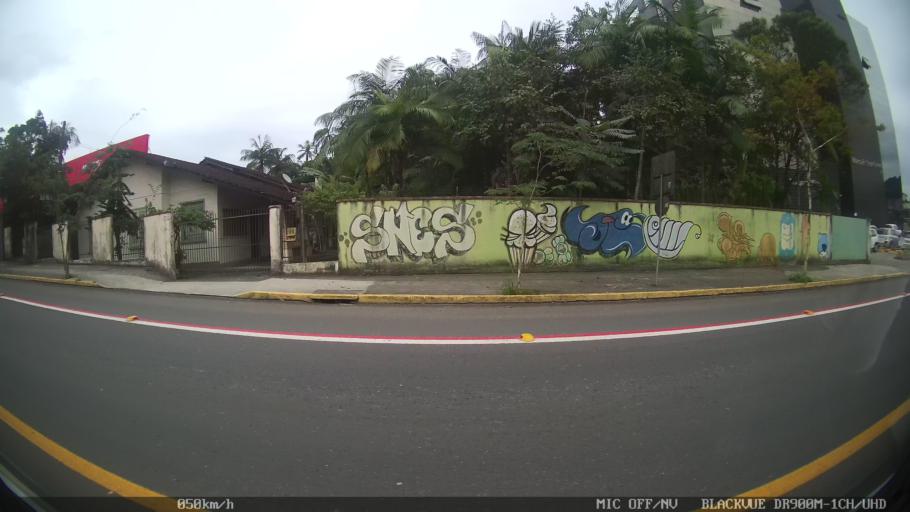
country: BR
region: Santa Catarina
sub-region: Joinville
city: Joinville
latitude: -26.2979
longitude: -48.8645
